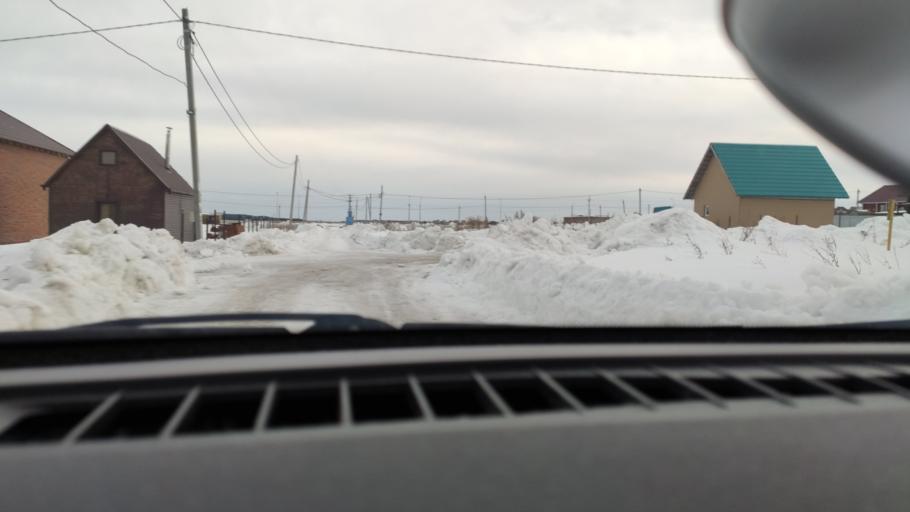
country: RU
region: Perm
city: Kultayevo
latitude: 57.8685
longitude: 55.8660
